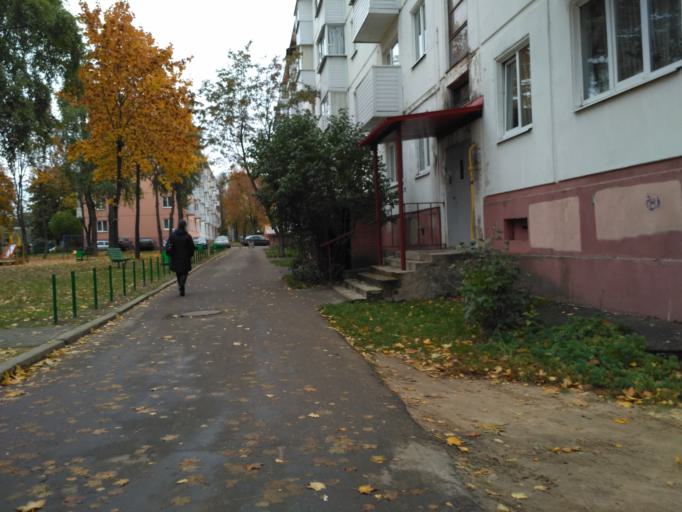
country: BY
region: Minsk
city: Horad Barysaw
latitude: 54.2172
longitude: 28.5063
